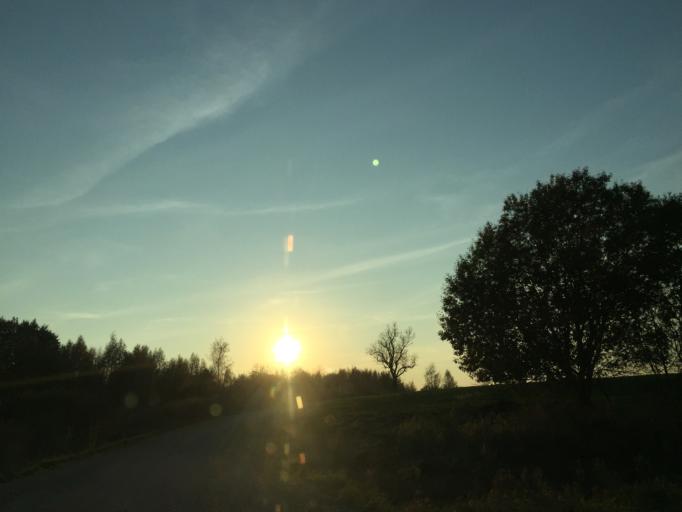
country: LV
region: Vainode
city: Vainode
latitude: 56.4895
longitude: 21.7773
